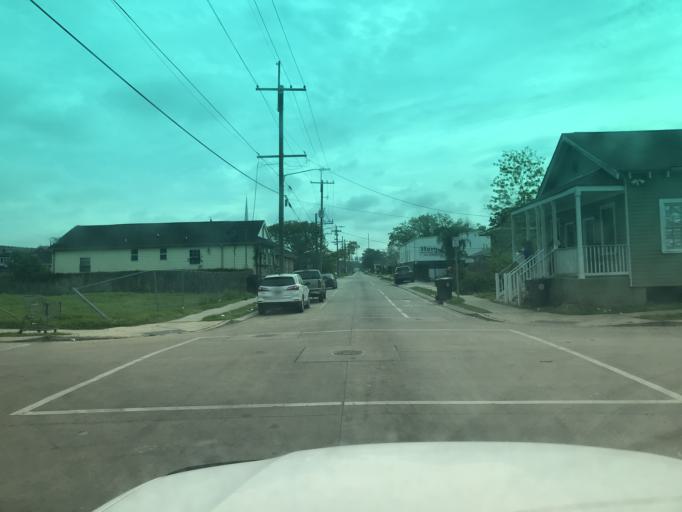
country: US
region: Louisiana
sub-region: Orleans Parish
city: New Orleans
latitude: 29.9789
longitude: -90.0542
